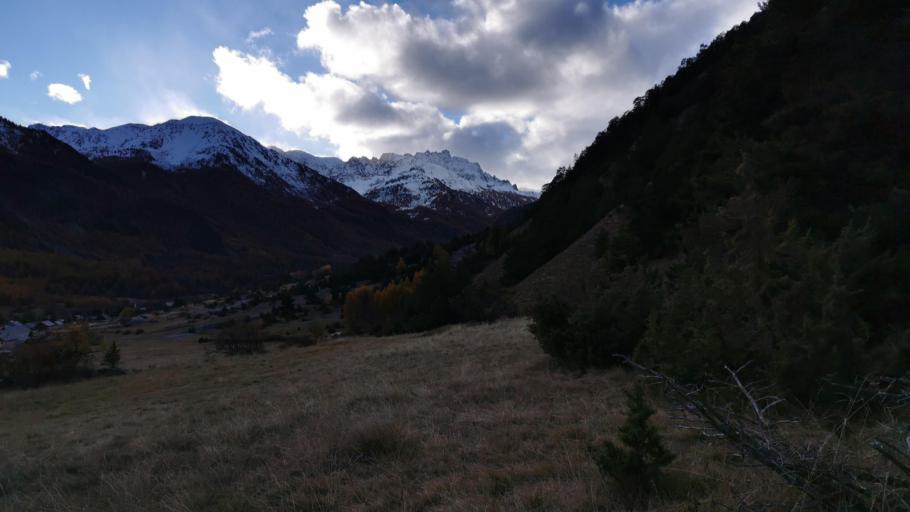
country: IT
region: Piedmont
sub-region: Provincia di Torino
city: Bardonecchia
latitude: 45.0235
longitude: 6.6326
